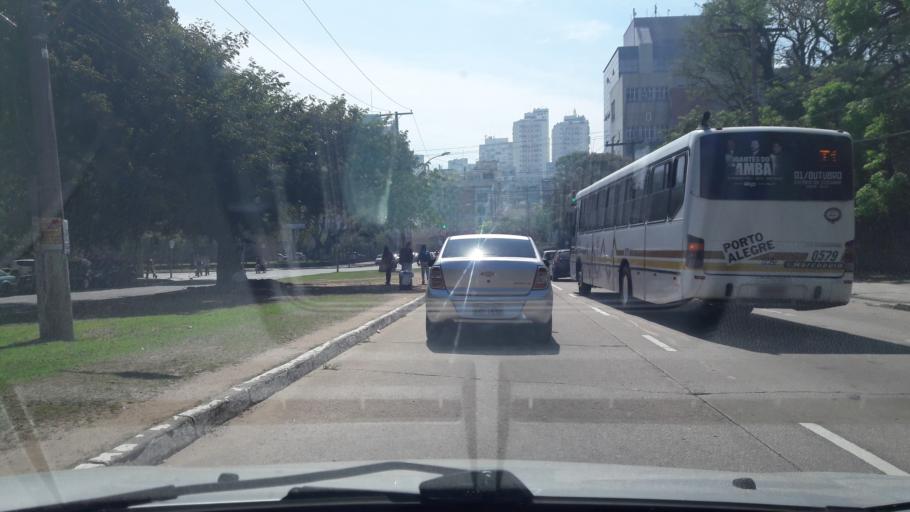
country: BR
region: Rio Grande do Sul
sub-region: Porto Alegre
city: Porto Alegre
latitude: -30.0381
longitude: -51.2327
